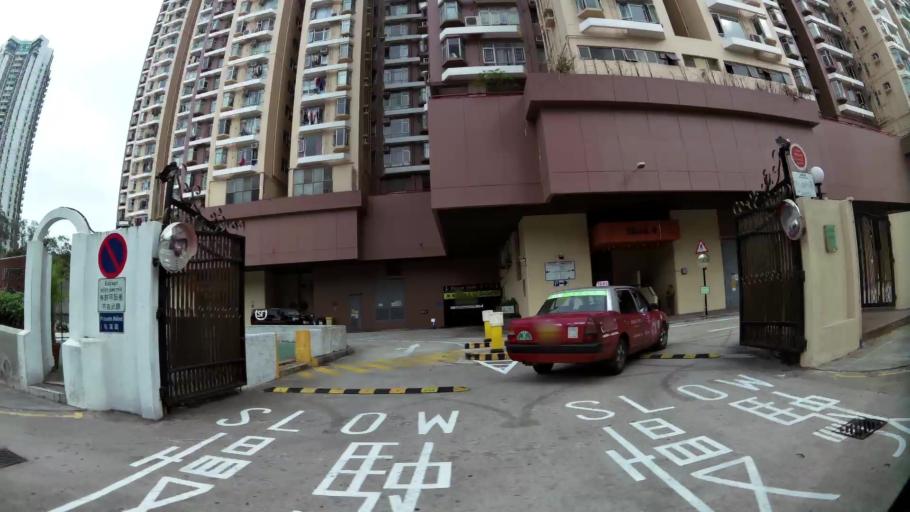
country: HK
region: Sha Tin
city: Sha Tin
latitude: 22.3983
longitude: 114.2002
